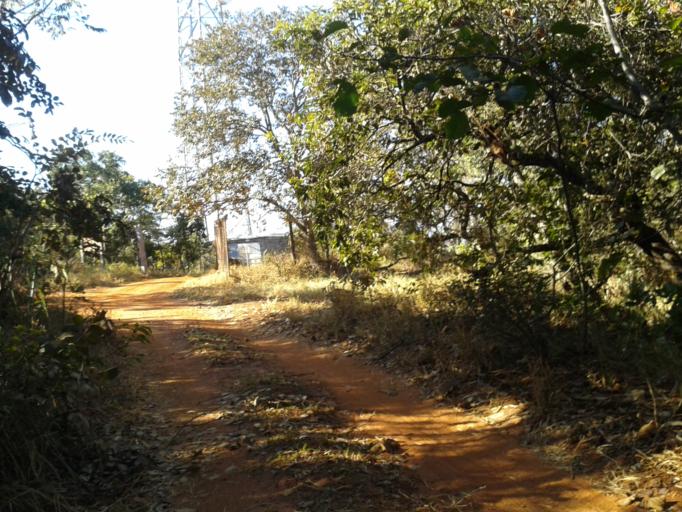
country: BR
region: Minas Gerais
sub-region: Capinopolis
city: Capinopolis
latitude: -18.7618
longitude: -49.5392
